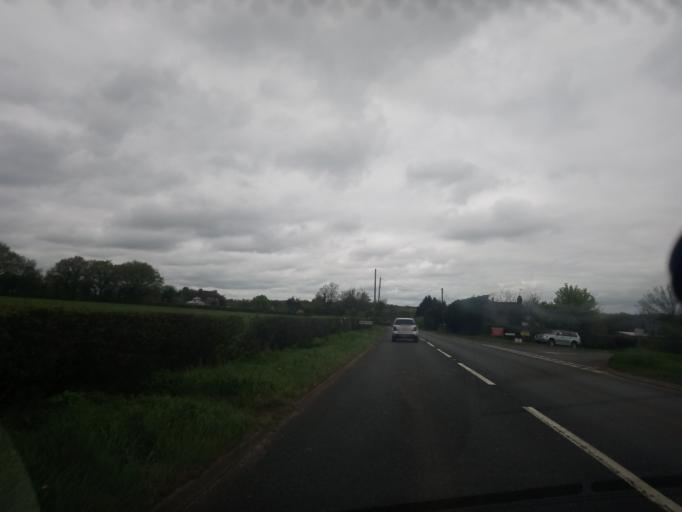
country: GB
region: England
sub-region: Telford and Wrekin
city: Chetwynd
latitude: 52.8249
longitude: -2.4532
